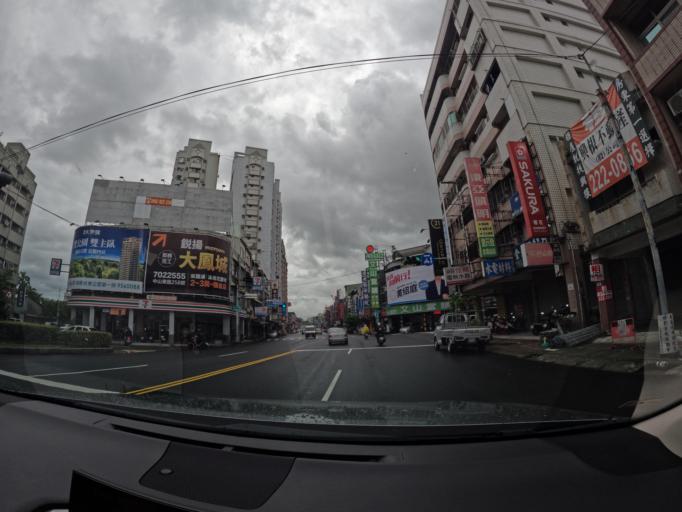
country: TW
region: Taiwan
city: Fengshan
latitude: 22.6293
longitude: 120.3398
